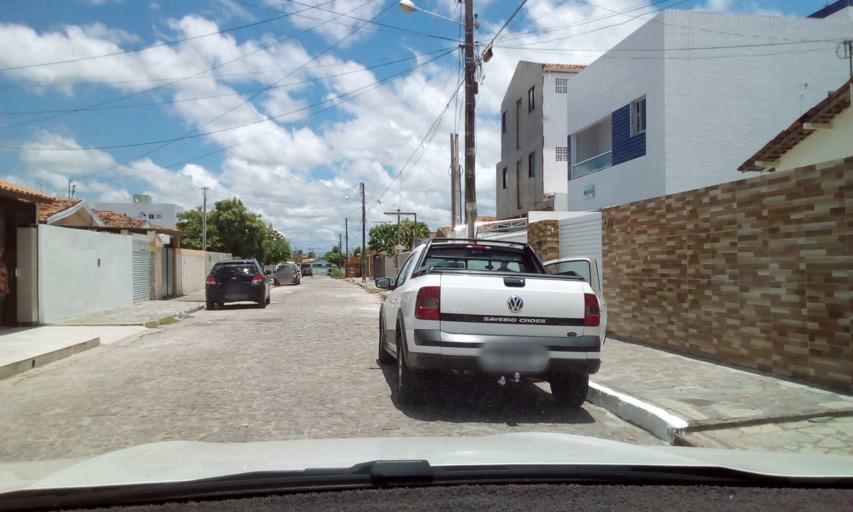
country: BR
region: Paraiba
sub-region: Joao Pessoa
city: Joao Pessoa
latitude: -7.1826
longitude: -34.8427
